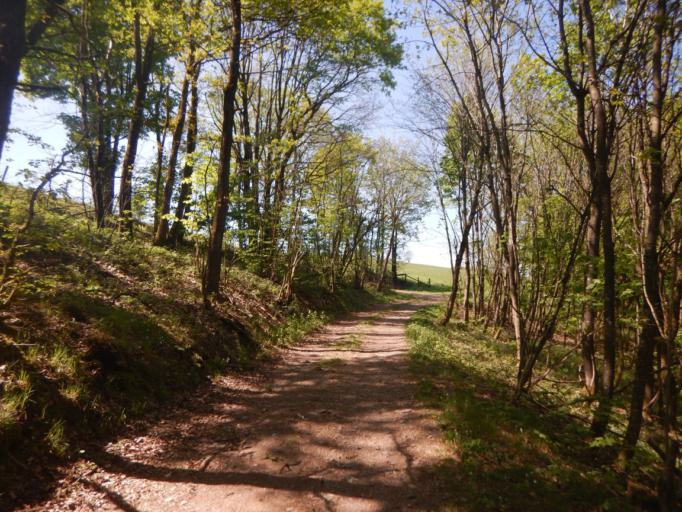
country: LU
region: Diekirch
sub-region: Canton de Diekirch
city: Bourscheid
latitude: 49.9040
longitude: 6.0715
